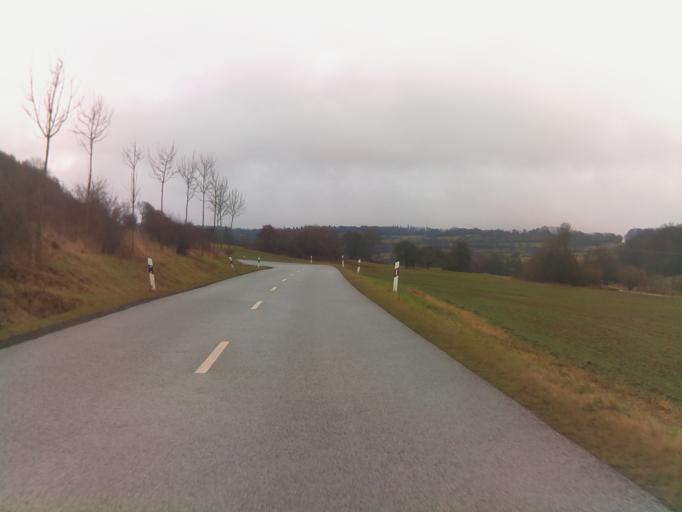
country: DE
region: Hesse
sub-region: Regierungsbezirk Giessen
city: Schotten
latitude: 50.5638
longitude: 9.0857
